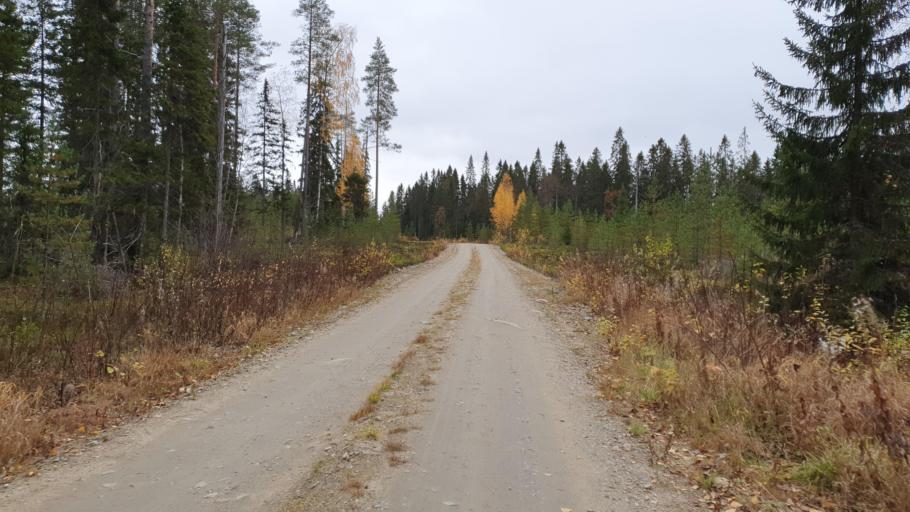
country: FI
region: Kainuu
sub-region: Kehys-Kainuu
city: Kuhmo
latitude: 64.4514
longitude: 29.6089
